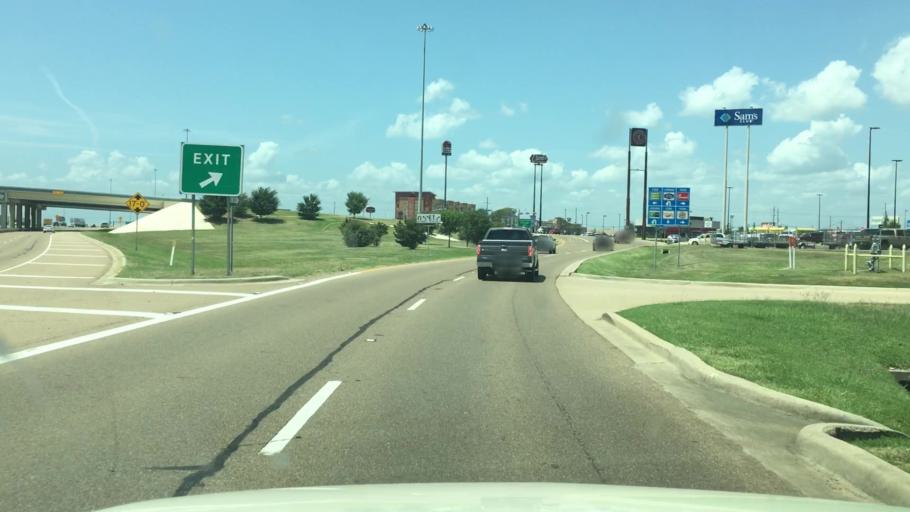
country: US
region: Texas
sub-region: Bowie County
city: Wake Village
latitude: 33.4578
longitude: -94.0850
